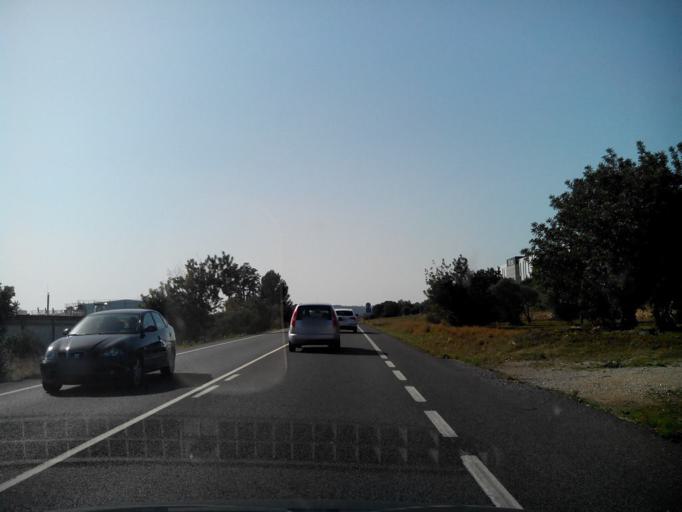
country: ES
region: Catalonia
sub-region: Provincia de Tarragona
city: Alcover
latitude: 41.2781
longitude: 1.1808
